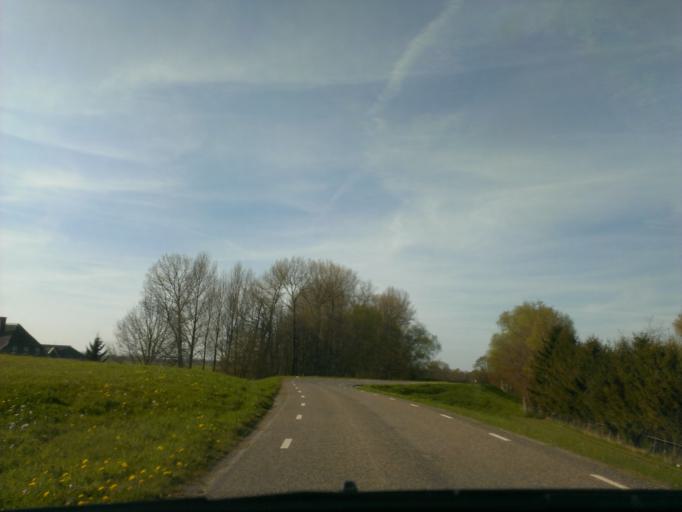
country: NL
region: Overijssel
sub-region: Gemeente Olst-Wijhe
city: Olst
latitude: 52.2975
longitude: 6.0949
